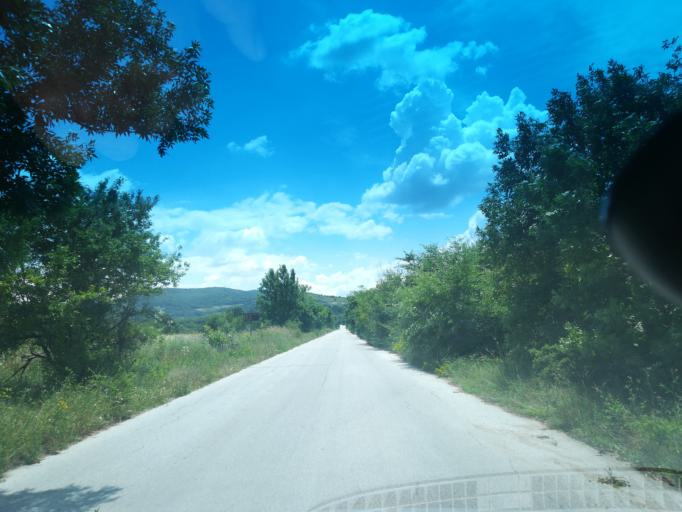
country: BG
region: Khaskovo
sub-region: Obshtina Mineralni Bani
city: Mineralni Bani
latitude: 41.9921
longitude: 25.2407
